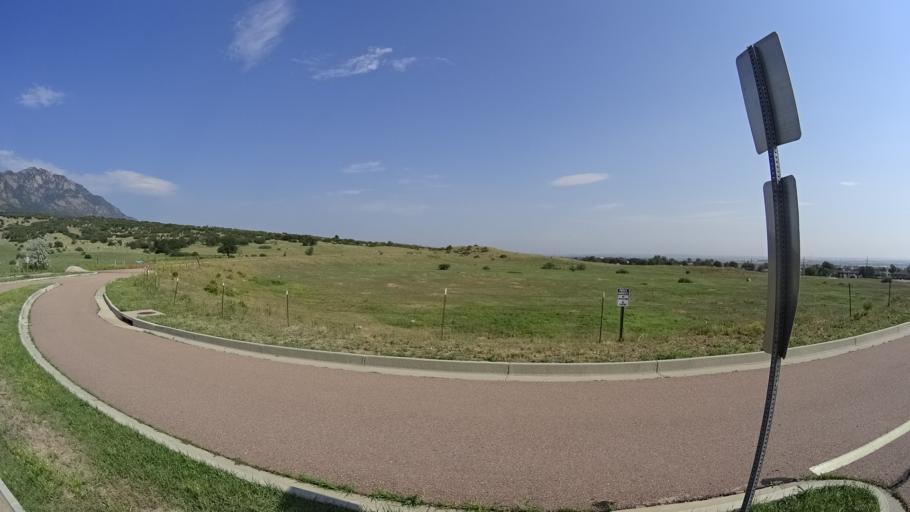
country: US
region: Colorado
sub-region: El Paso County
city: Fort Carson
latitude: 38.7378
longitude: -104.8110
